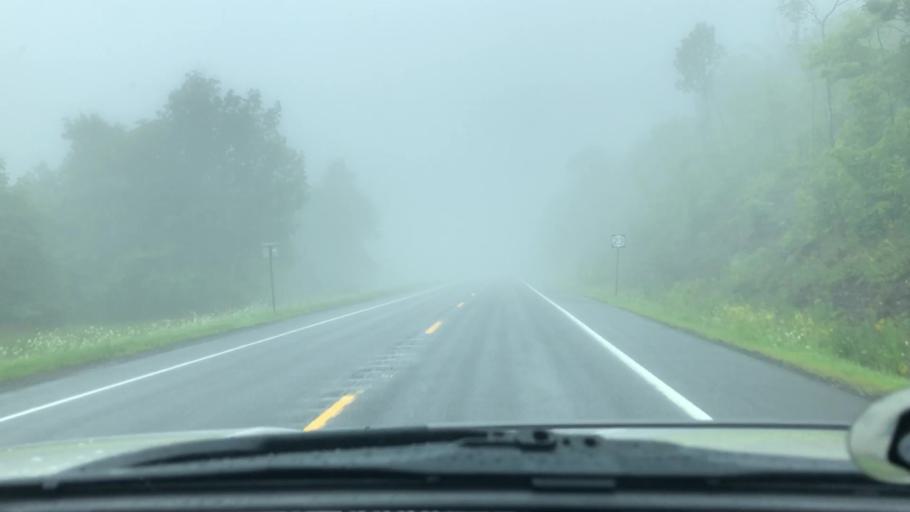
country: US
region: New York
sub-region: Greene County
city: Cairo
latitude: 42.3336
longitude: -74.1637
